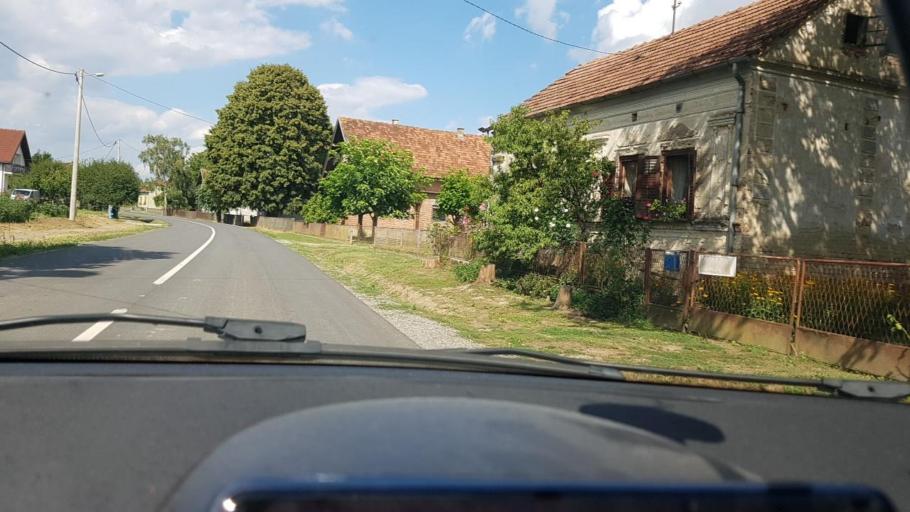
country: HR
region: Bjelovarsko-Bilogorska
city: Zdralovi
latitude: 45.8481
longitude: 16.9756
